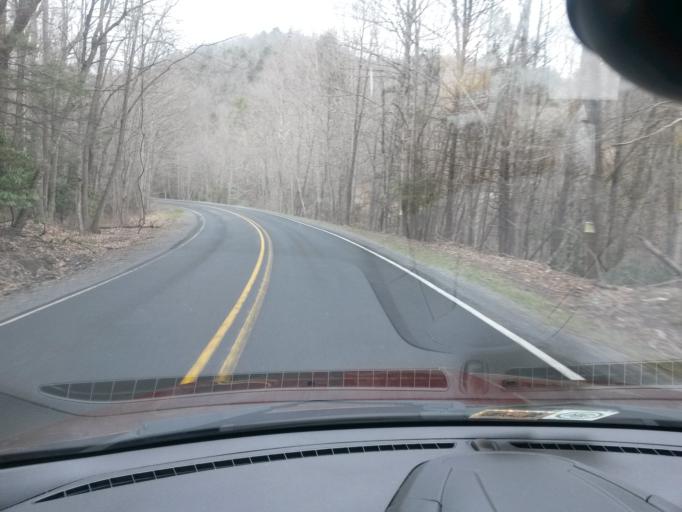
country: US
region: Virginia
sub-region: Bath County
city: Warm Springs
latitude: 38.1662
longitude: -79.7335
